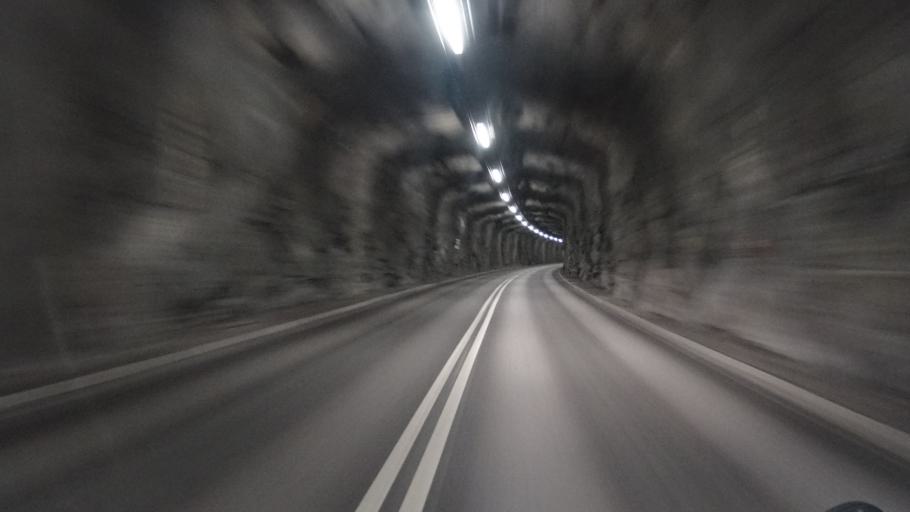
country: SE
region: Stockholm
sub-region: Nynashamns Kommun
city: Nynashamn
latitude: 58.9628
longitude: 18.0242
